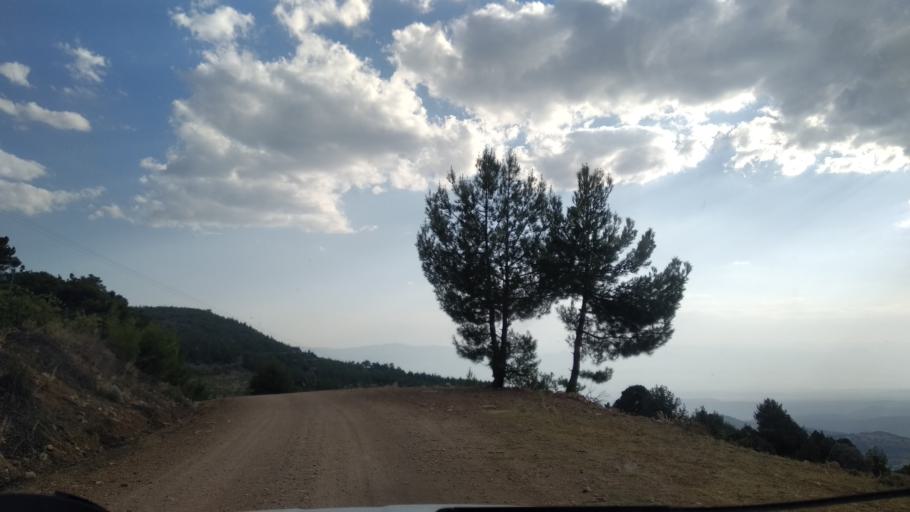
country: TR
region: Mersin
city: Sarikavak
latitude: 36.5920
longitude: 33.6789
